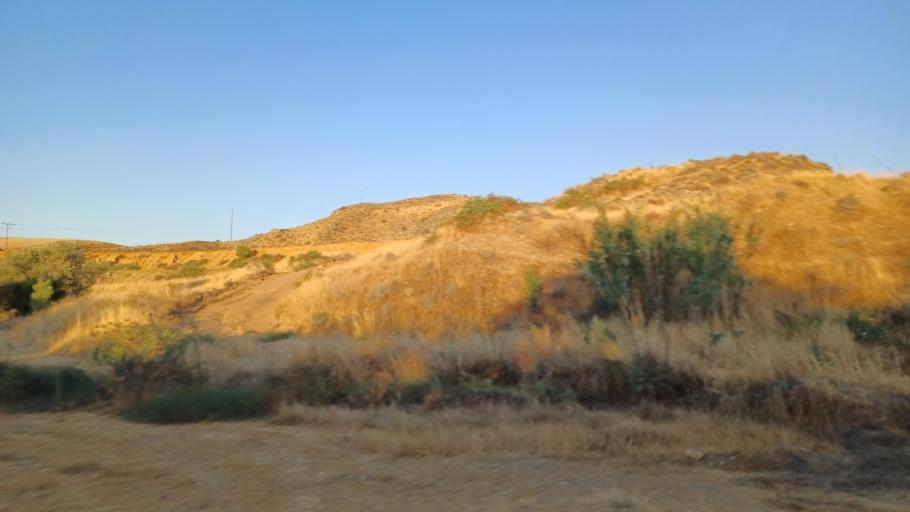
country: CY
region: Larnaka
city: Troulloi
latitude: 35.0298
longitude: 33.6274
